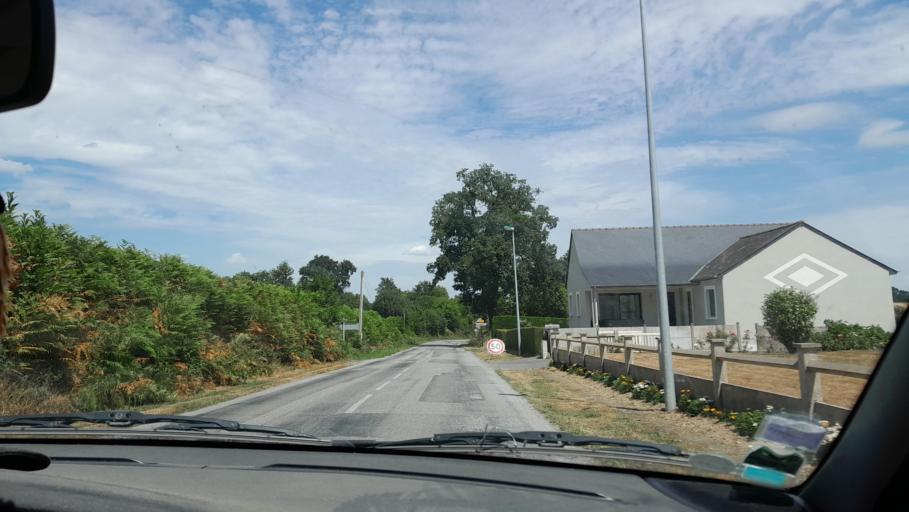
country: FR
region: Brittany
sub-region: Departement d'Ille-et-Vilaine
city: Le Pertre
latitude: 48.0382
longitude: -1.0366
